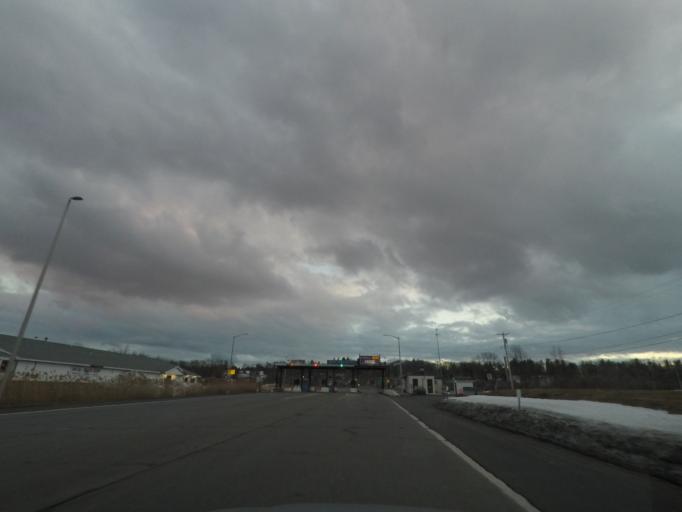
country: US
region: New York
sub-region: Montgomery County
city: Fonda
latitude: 42.9479
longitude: -74.3586
